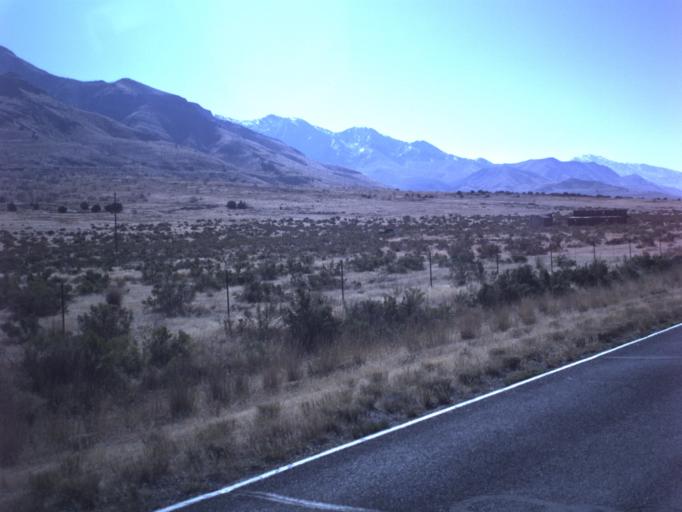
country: US
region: Utah
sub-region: Tooele County
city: Grantsville
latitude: 40.6795
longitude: -112.6716
